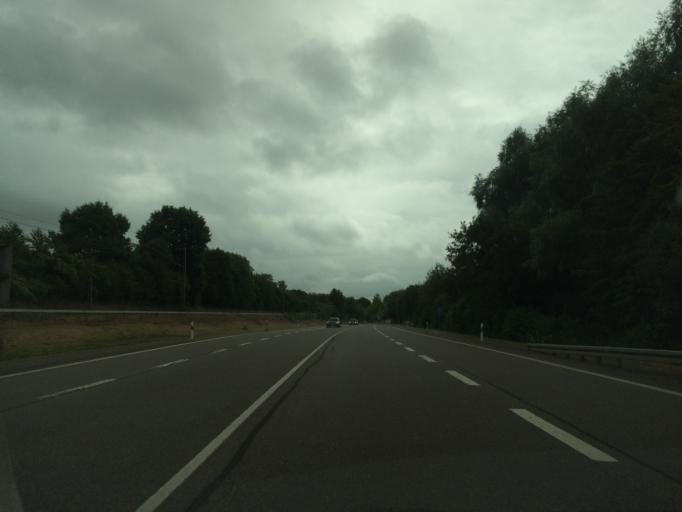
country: DE
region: Saarland
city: Merzig
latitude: 49.4210
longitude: 6.6363
